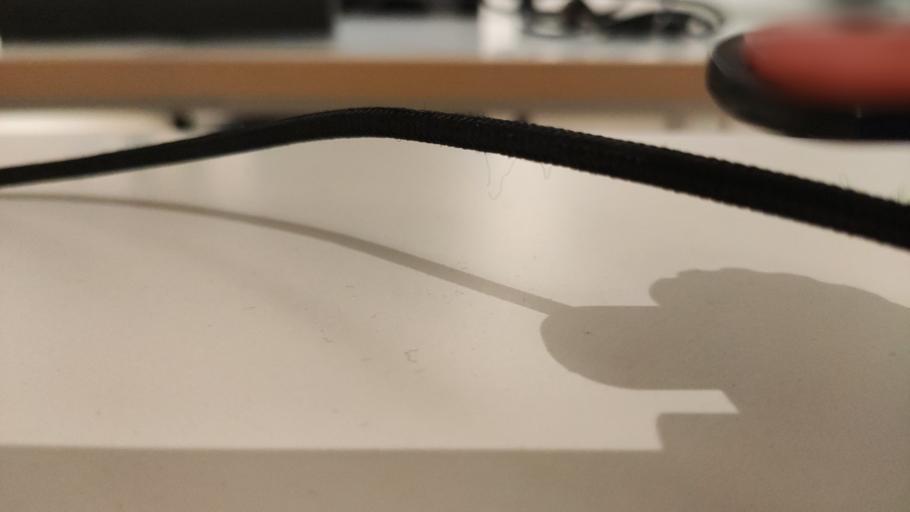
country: RU
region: Kaluga
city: Belousovo
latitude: 55.1418
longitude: 36.7736
